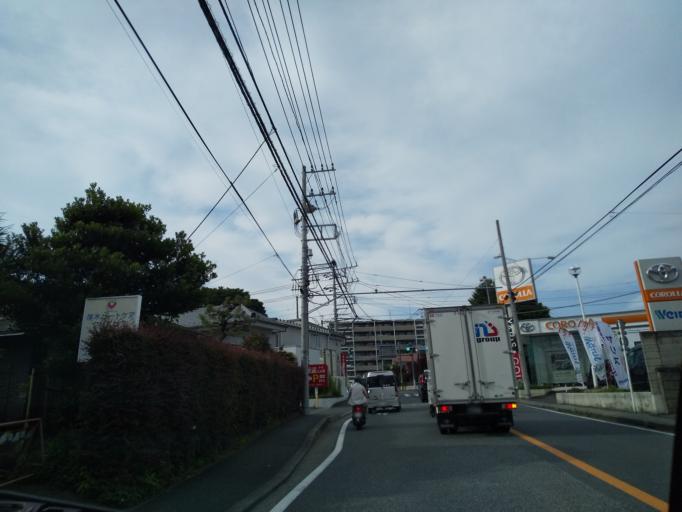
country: JP
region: Kanagawa
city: Atsugi
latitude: 35.4779
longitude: 139.3412
